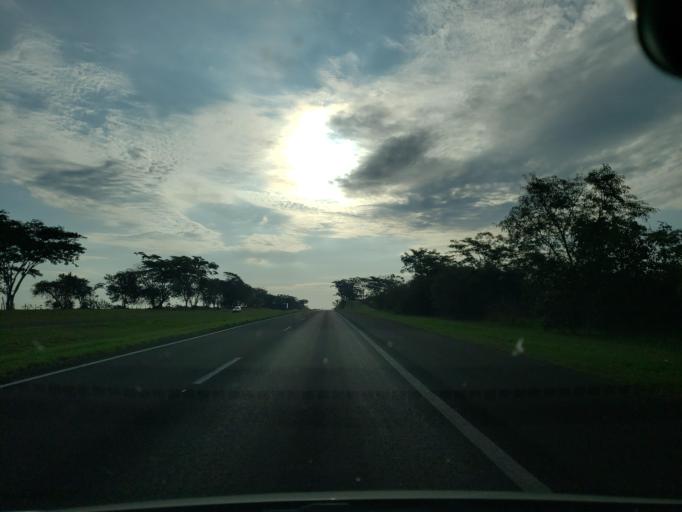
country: BR
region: Sao Paulo
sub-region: Mirandopolis
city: Mirandopolis
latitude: -21.1134
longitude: -51.0196
